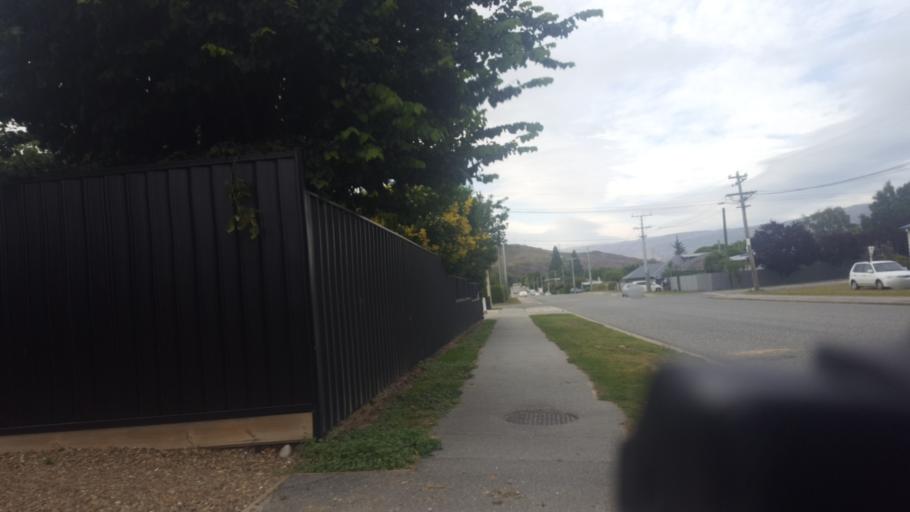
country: NZ
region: Otago
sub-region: Queenstown-Lakes District
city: Wanaka
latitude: -45.0424
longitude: 169.2120
